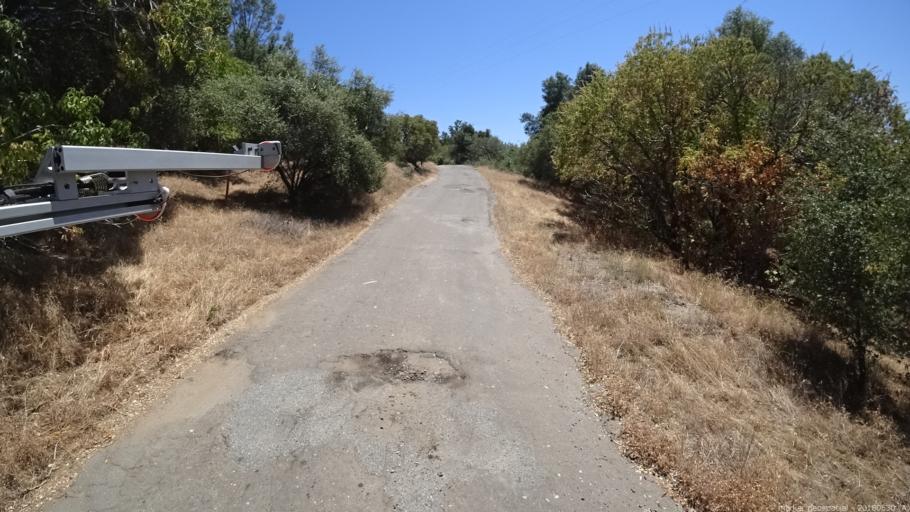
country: US
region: California
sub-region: Fresno County
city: Auberry
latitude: 37.1728
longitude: -119.4564
